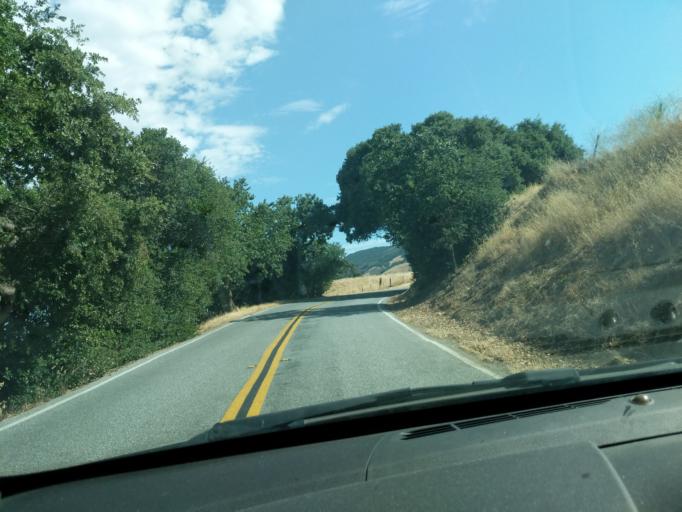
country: US
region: California
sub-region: Santa Clara County
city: Gilroy
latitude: 37.0671
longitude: -121.5225
